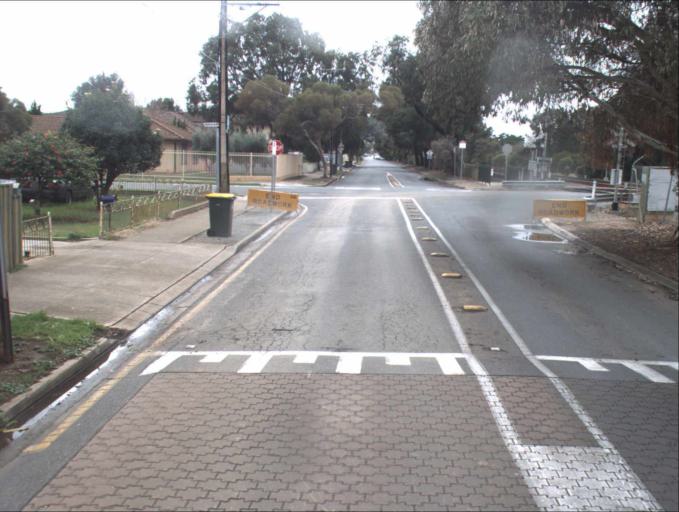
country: AU
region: South Australia
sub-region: Prospect
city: Prospect
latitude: -34.8886
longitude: 138.5833
